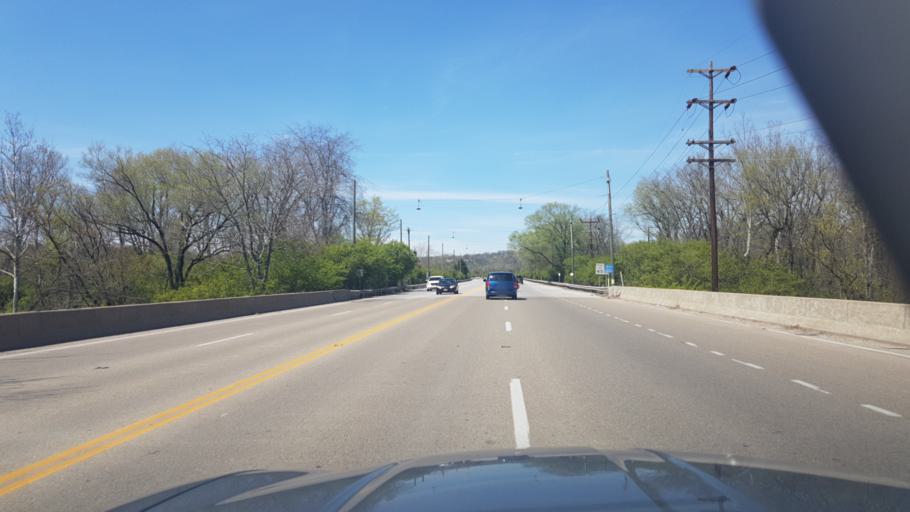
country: US
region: Ohio
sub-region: Hamilton County
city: Turpin Hills
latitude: 39.1094
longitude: -84.4016
